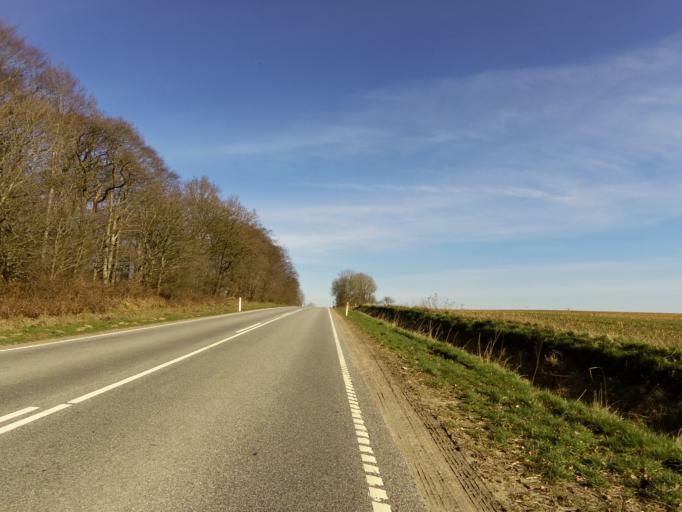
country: DK
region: South Denmark
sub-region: Vejen Kommune
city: Rodding
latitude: 55.3584
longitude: 9.1471
